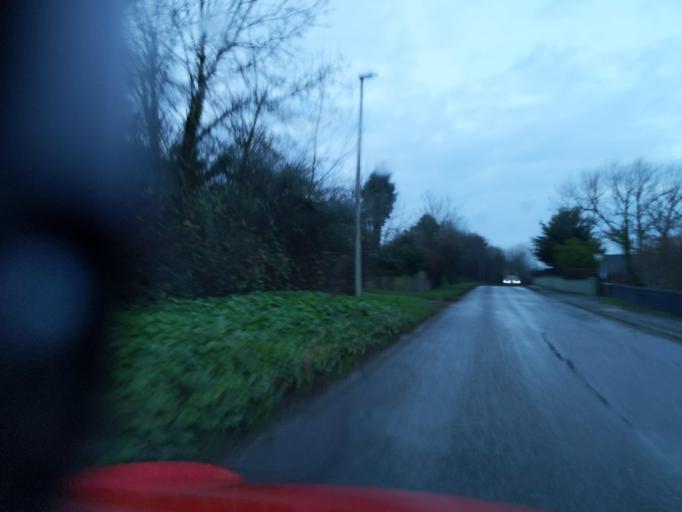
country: GB
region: England
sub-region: Devon
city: Wembury
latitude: 50.3359
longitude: -4.0722
